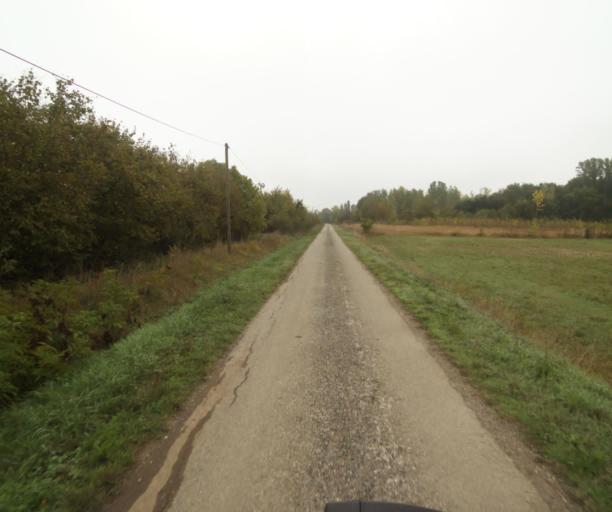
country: FR
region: Midi-Pyrenees
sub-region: Departement du Tarn-et-Garonne
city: Orgueil
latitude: 43.9069
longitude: 1.4169
